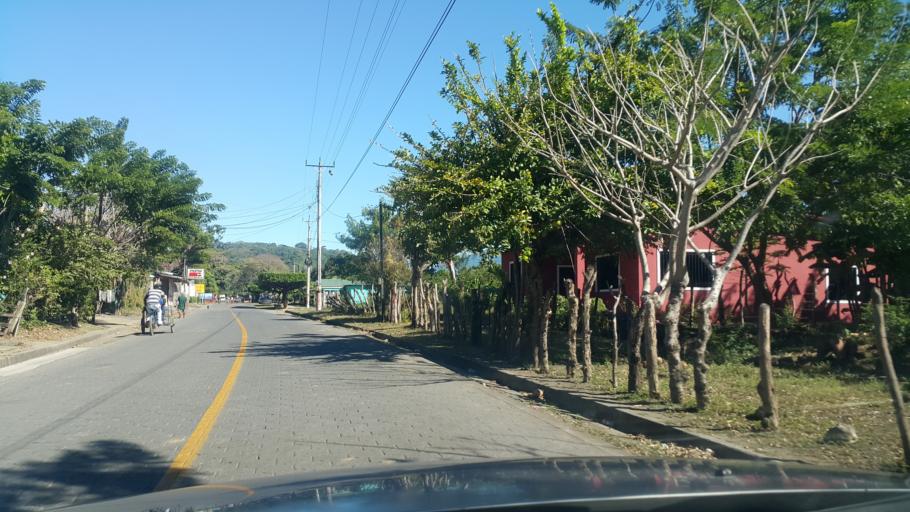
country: NI
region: Rivas
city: Moyogalpa
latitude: 11.4856
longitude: -85.6462
